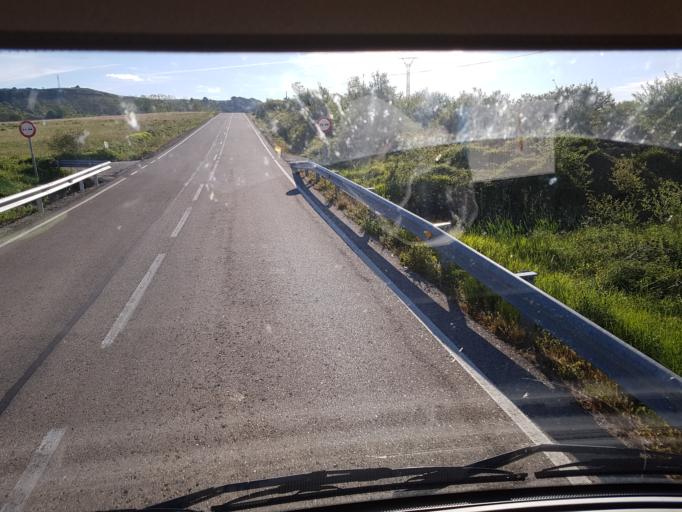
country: ES
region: Castille and Leon
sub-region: Provincia de Burgos
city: Arija
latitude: 42.9767
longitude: -3.8748
